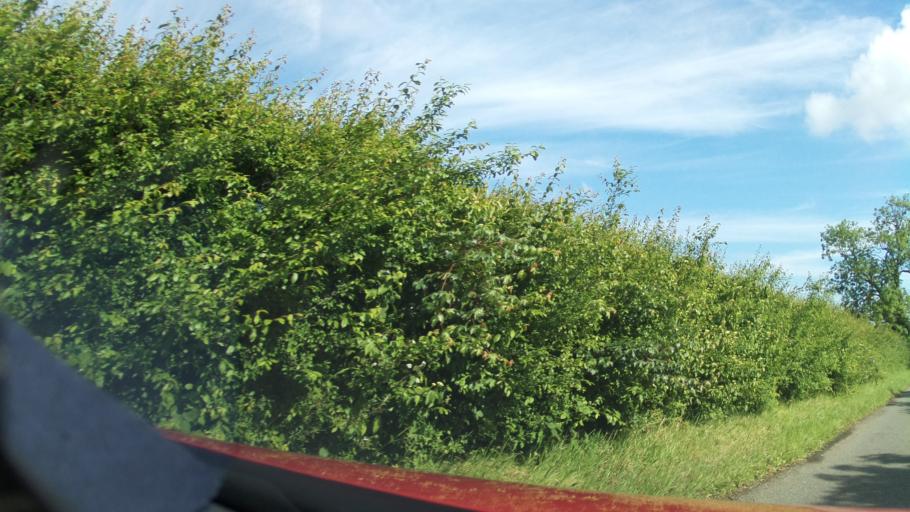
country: GB
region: England
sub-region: Lincolnshire
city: Skellingthorpe
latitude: 53.1344
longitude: -0.6337
